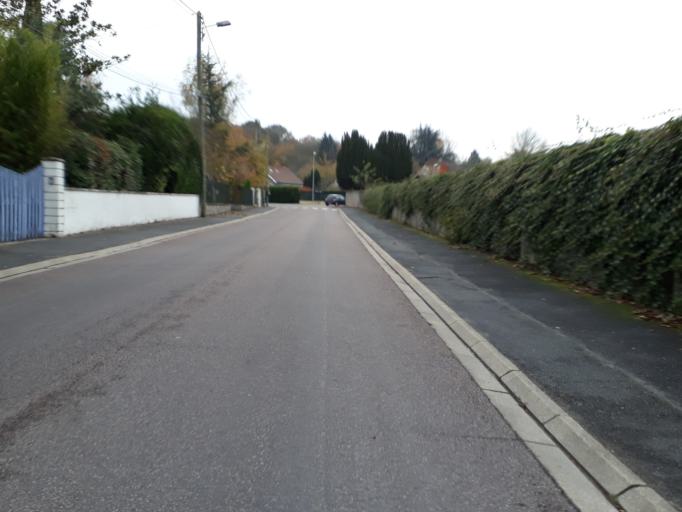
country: FR
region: Ile-de-France
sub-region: Departement de Seine-et-Marne
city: Bois-le-Roi
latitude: 48.4747
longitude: 2.7049
